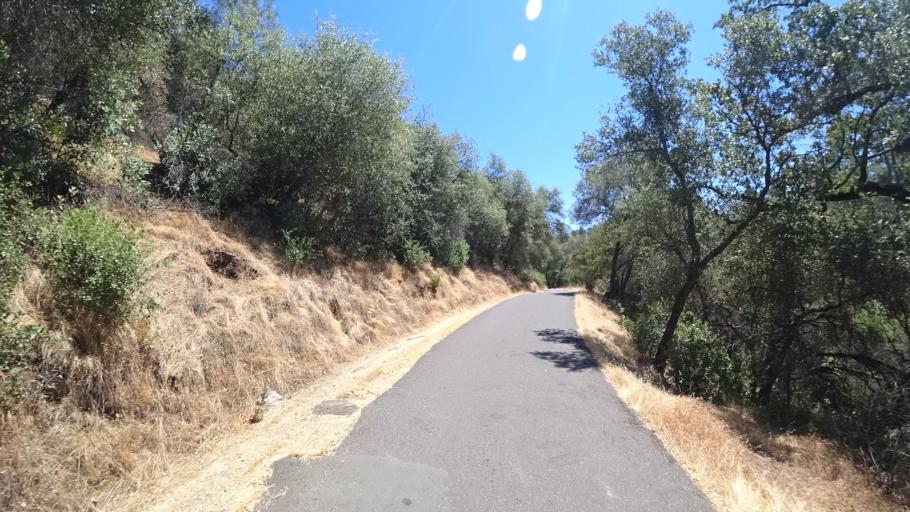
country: US
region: California
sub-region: Calaveras County
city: Mountain Ranch
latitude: 38.1777
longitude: -120.5885
